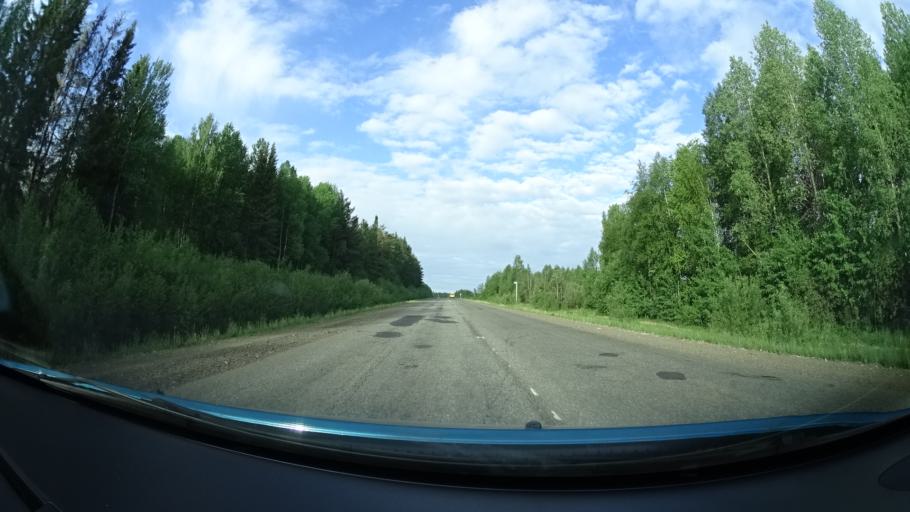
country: RU
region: Perm
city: Osa
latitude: 57.4463
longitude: 55.6460
